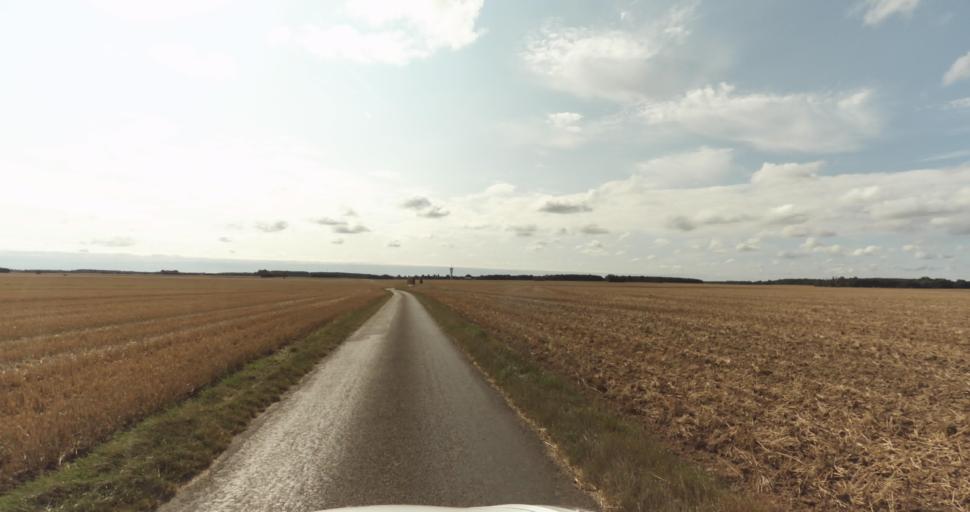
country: FR
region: Haute-Normandie
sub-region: Departement de l'Eure
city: Tillieres-sur-Avre
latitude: 48.7858
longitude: 1.0655
